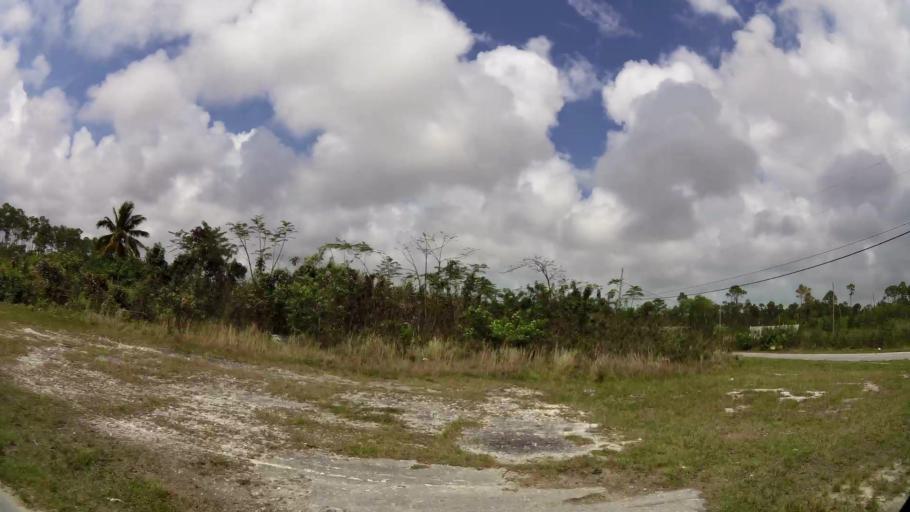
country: BS
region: Freeport
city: Lucaya
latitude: 26.5315
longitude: -78.6534
